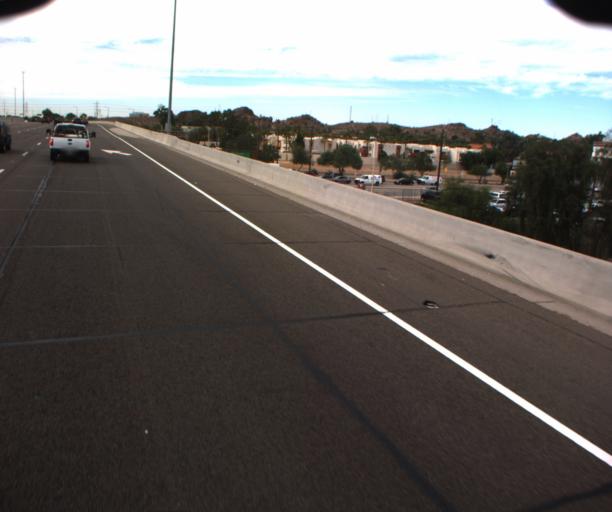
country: US
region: Arizona
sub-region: Maricopa County
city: Tempe
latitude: 33.4363
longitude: -111.9251
